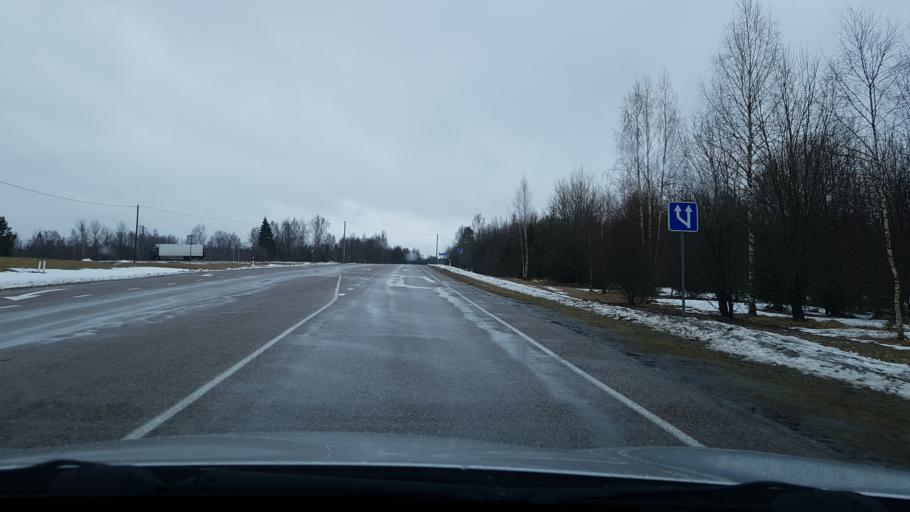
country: LV
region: Apes Novads
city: Ape
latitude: 57.7314
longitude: 26.7839
